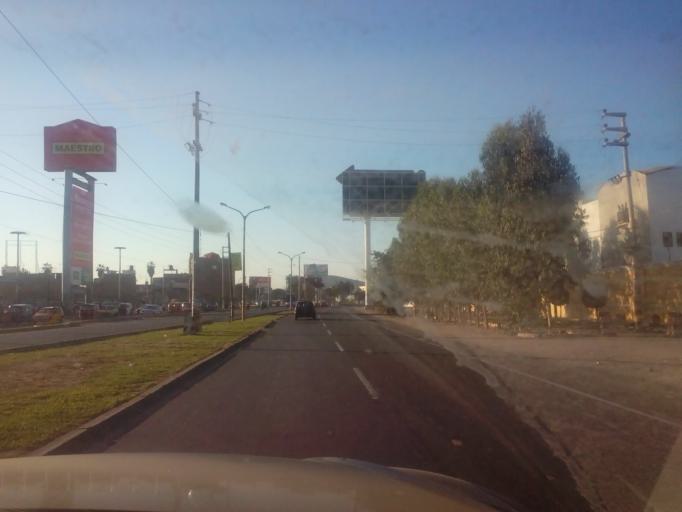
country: PE
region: Ica
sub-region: Provincia de Ica
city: Ica
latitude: -14.0745
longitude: -75.7384
